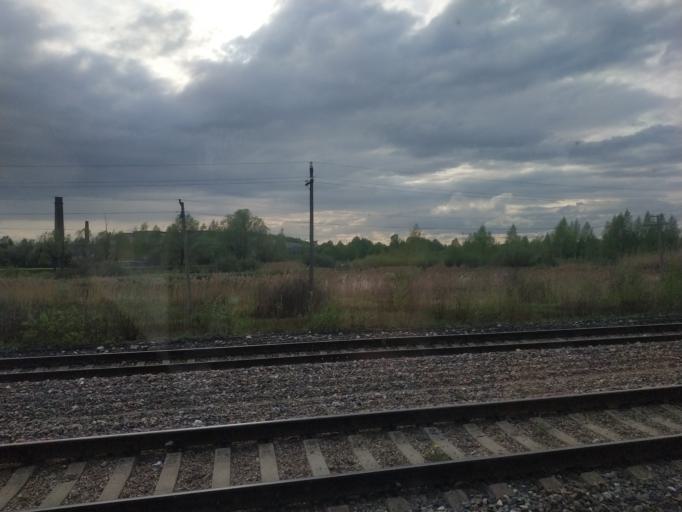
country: RU
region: Smolensk
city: Ugra
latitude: 54.7737
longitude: 34.3427
